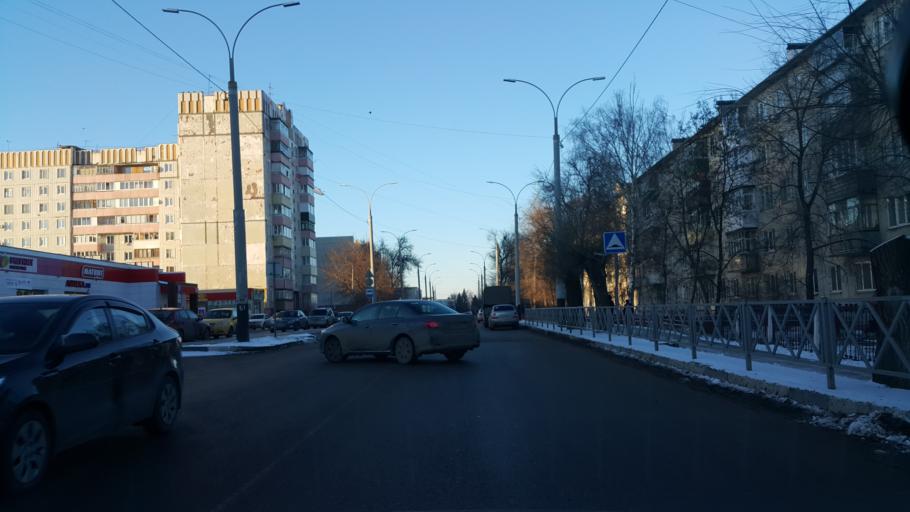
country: RU
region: Tambov
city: Pokrovo-Prigorodnoye
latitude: 52.7070
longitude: 41.3981
